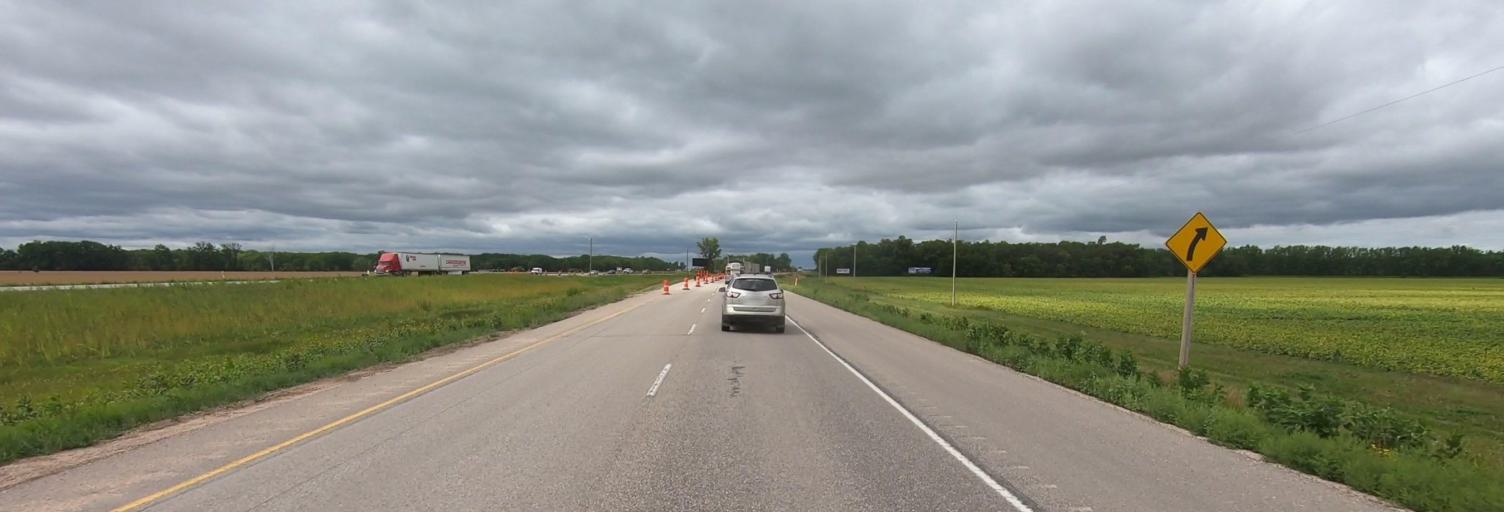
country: CA
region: Manitoba
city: Portage la Prairie
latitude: 49.9664
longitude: -98.0788
